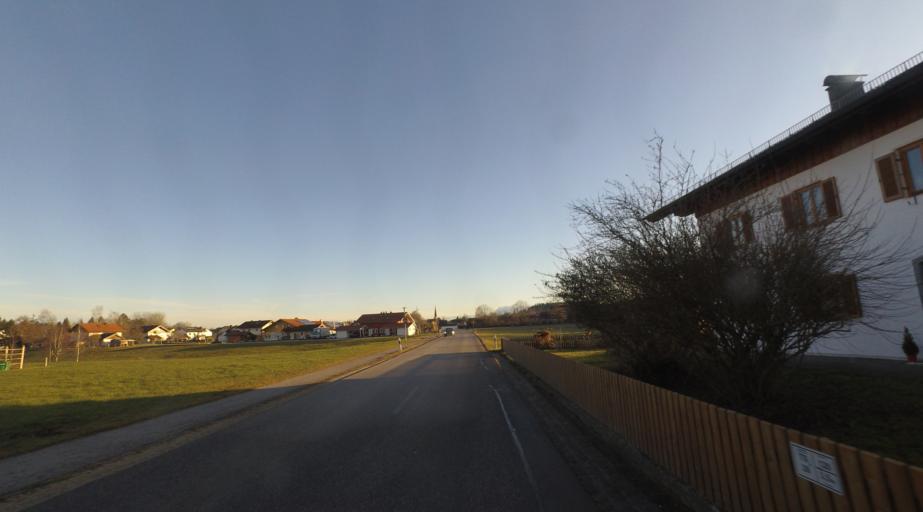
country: DE
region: Bavaria
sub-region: Upper Bavaria
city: Kirchanschoring
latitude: 47.9588
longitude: 12.8290
